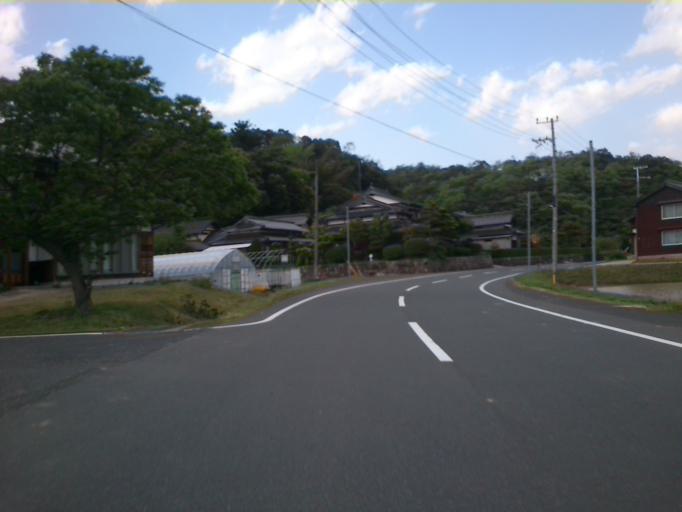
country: JP
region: Kyoto
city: Miyazu
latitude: 35.6948
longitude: 135.0983
